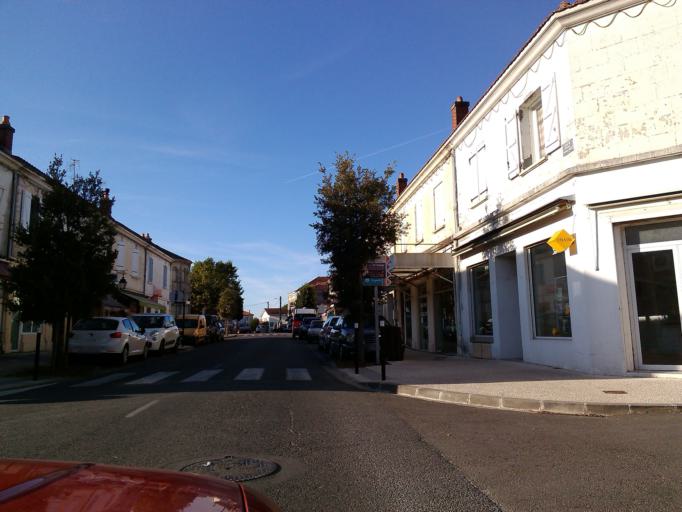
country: FR
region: Aquitaine
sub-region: Departement de la Gironde
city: Soulac-sur-Mer
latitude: 45.4299
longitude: -1.0351
